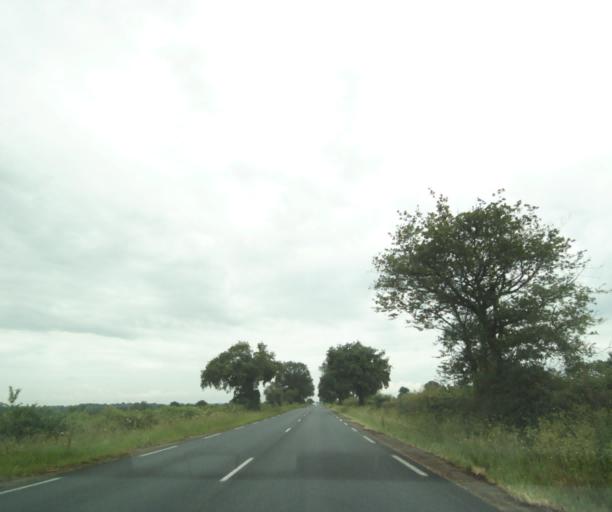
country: FR
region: Poitou-Charentes
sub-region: Departement des Deux-Sevres
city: Viennay
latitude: 46.7424
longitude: -0.2309
